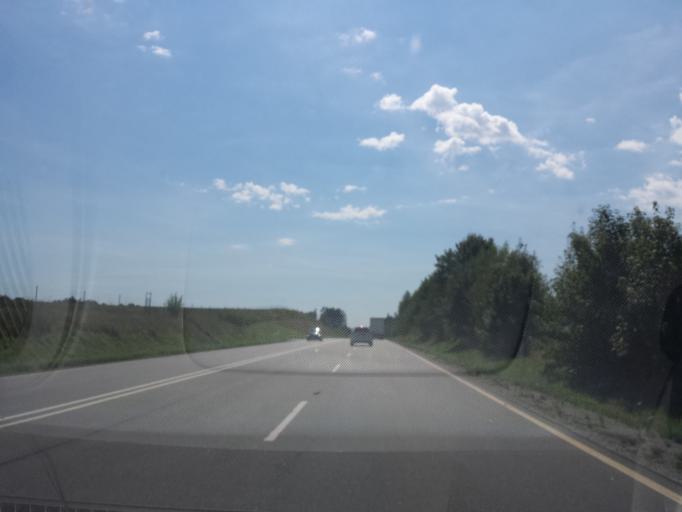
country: DE
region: Bavaria
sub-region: Lower Bavaria
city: Ascha
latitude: 48.9764
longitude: 12.6281
